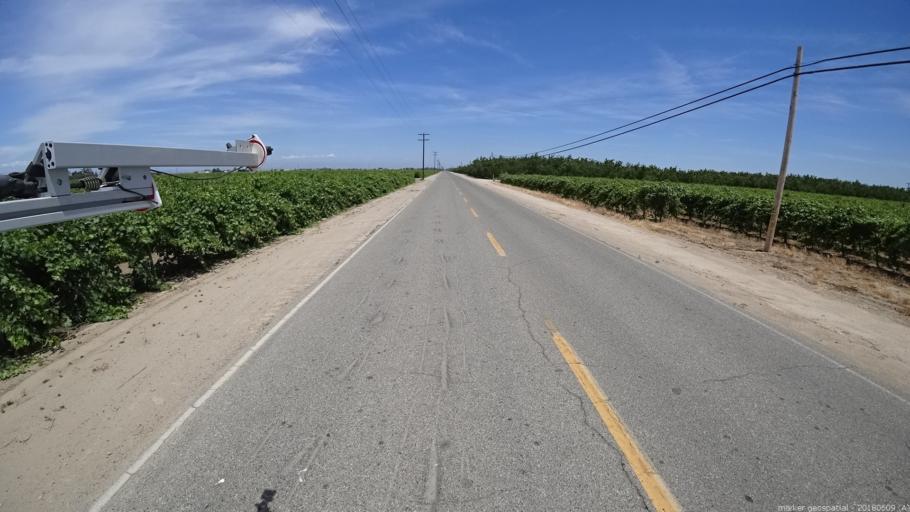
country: US
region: California
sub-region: Madera County
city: Parkwood
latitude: 36.9094
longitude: -120.0706
